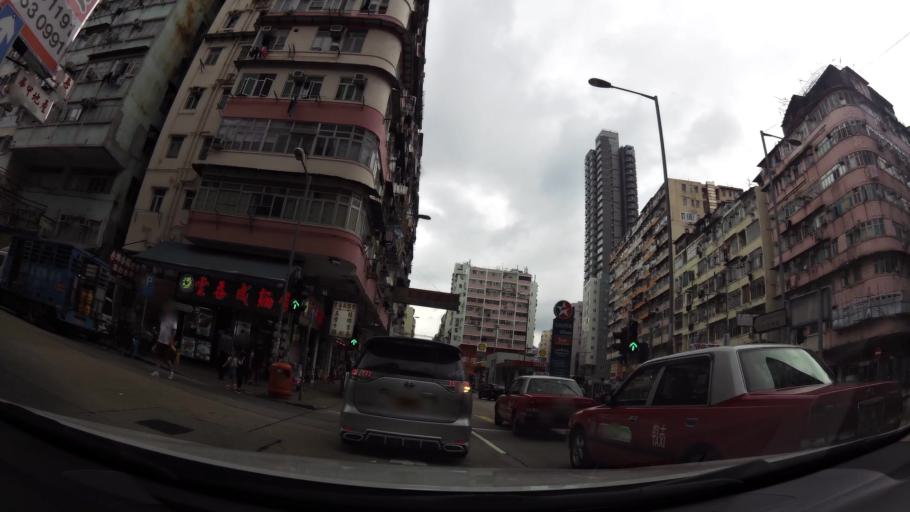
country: HK
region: Sham Shui Po
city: Sham Shui Po
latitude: 22.3304
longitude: 114.1659
